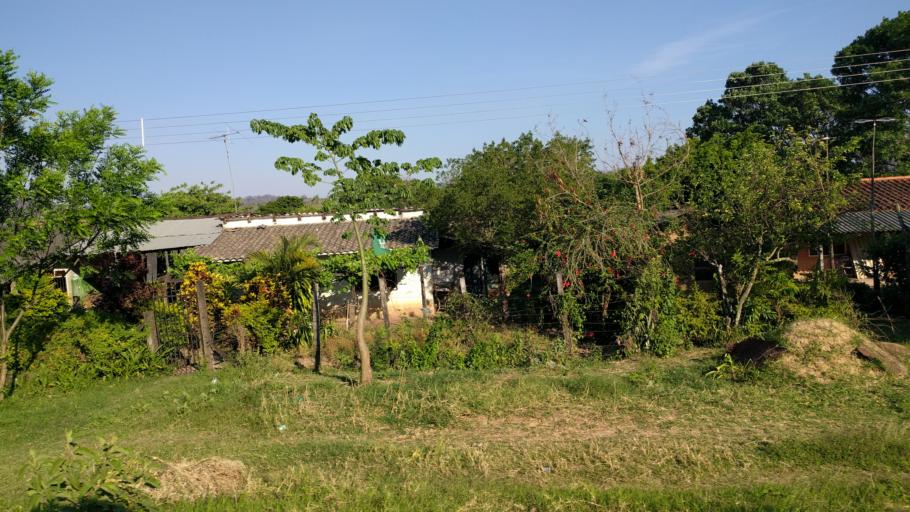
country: BO
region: Santa Cruz
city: Jorochito
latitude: -18.1334
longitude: -63.4720
